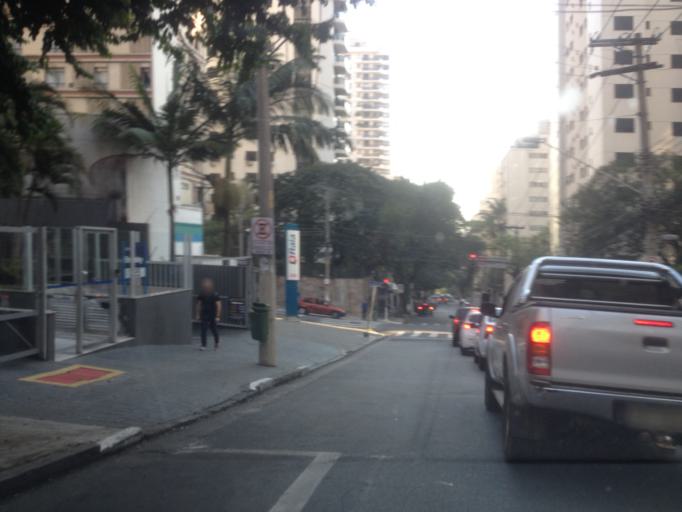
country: BR
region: Sao Paulo
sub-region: Sao Paulo
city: Sao Paulo
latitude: -23.5604
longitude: -46.6607
